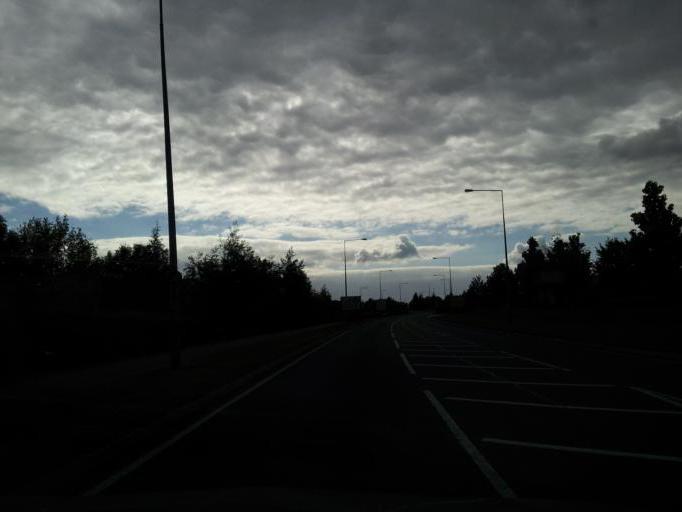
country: GB
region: England
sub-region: Milton Keynes
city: Shenley Church End
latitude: 52.0060
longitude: -0.8027
